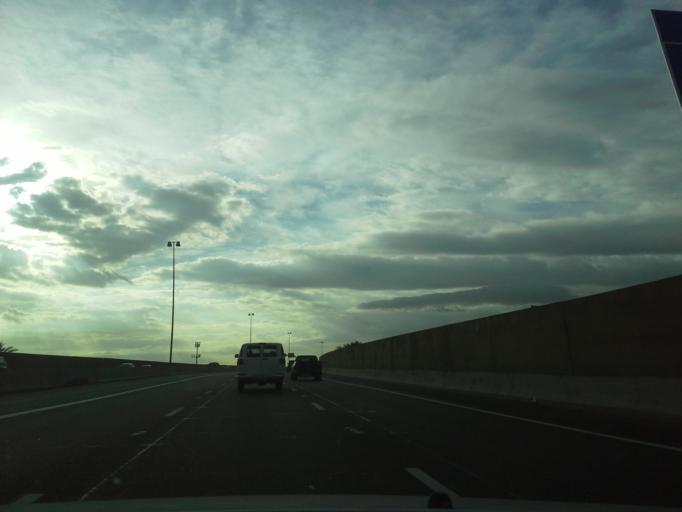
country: US
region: Arizona
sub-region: Maricopa County
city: Phoenix
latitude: 33.4839
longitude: -112.0401
